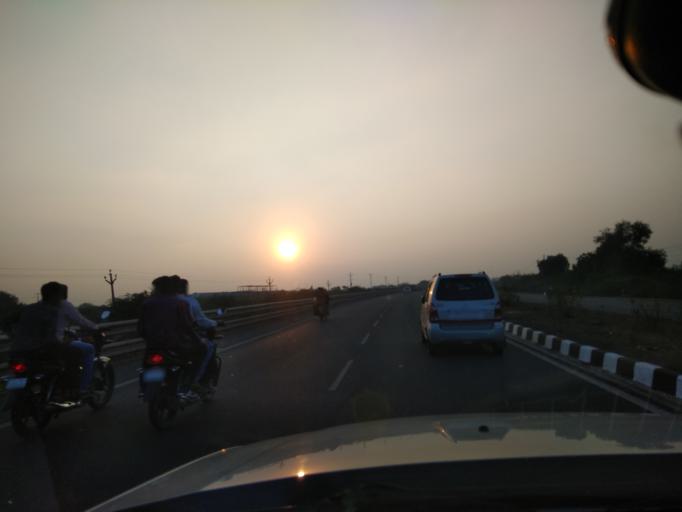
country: IN
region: Gujarat
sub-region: Jamnagar
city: Bedi
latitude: 22.4429
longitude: 69.9970
